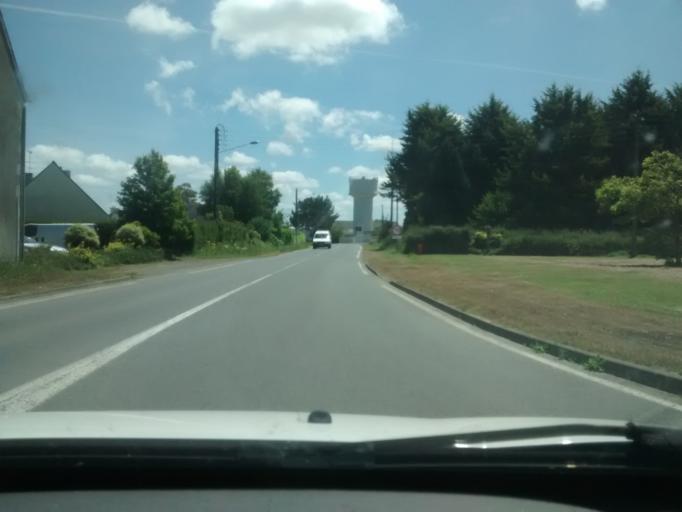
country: FR
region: Brittany
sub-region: Departement des Cotes-d'Armor
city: Louannec
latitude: 48.7848
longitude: -3.3962
